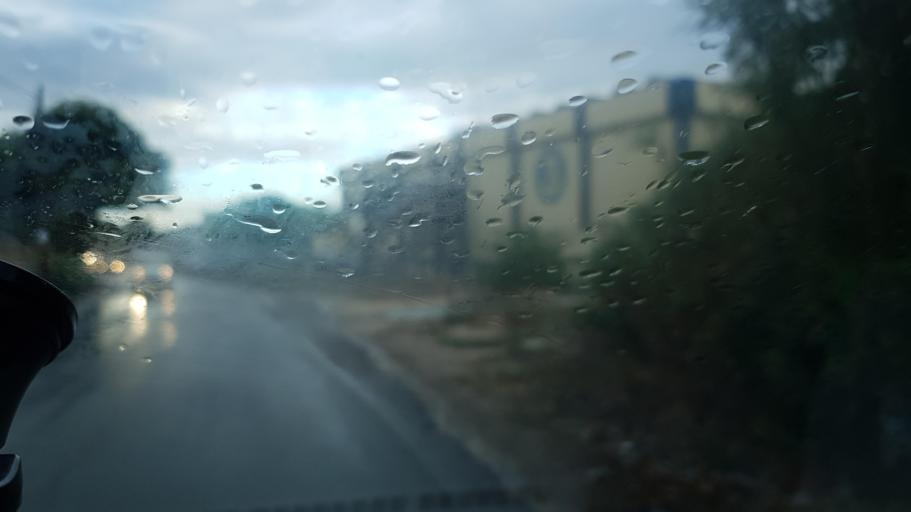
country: IT
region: Apulia
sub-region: Provincia di Lecce
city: Giorgilorio
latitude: 40.3775
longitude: 18.1474
